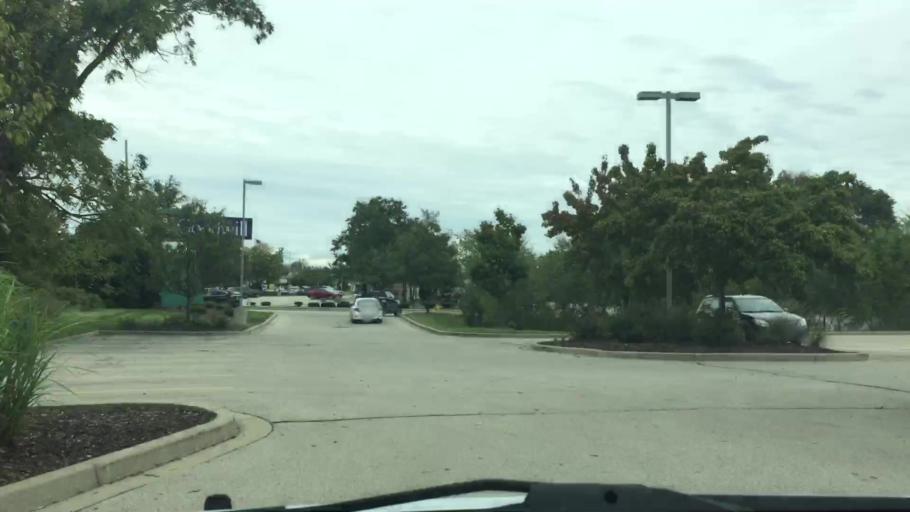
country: US
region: Wisconsin
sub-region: Waukesha County
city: Pewaukee
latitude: 43.0413
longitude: -88.2601
